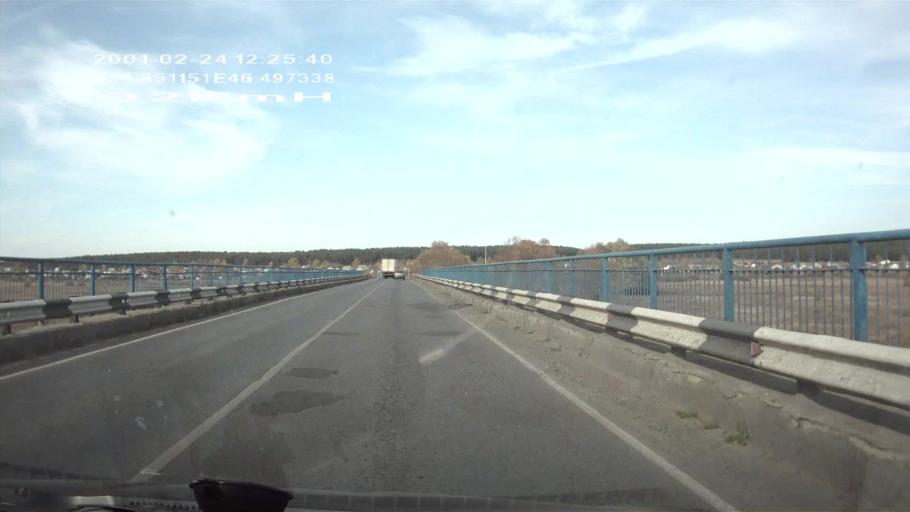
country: RU
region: Chuvashia
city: Alatyr'
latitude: 54.8512
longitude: 46.4973
